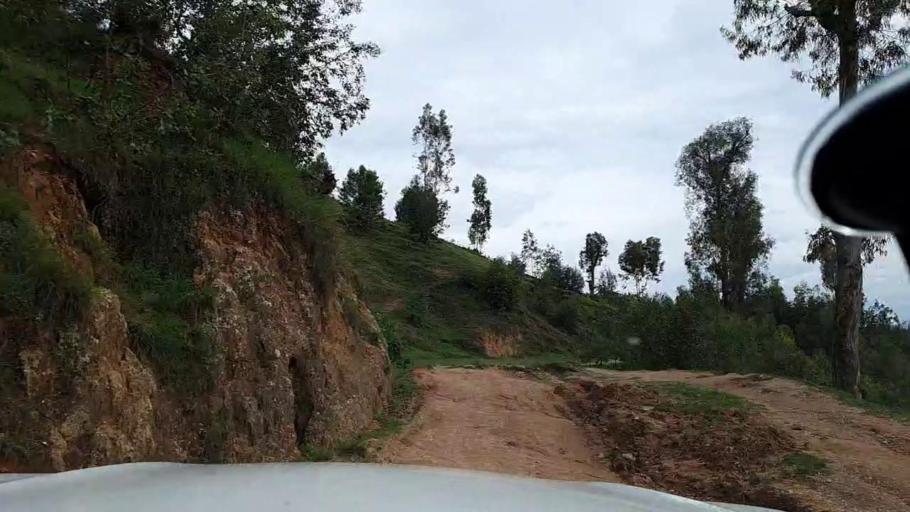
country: RW
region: Southern Province
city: Gitarama
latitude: -2.1252
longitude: 29.6545
